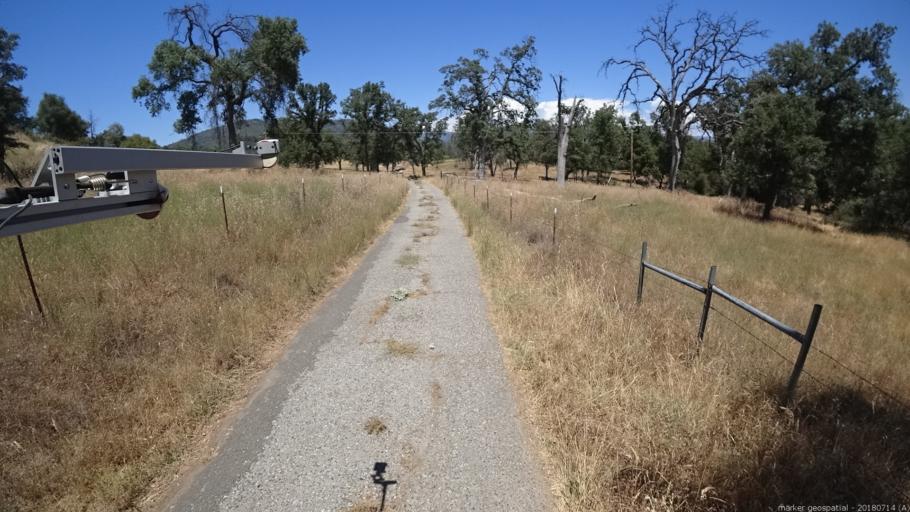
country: US
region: California
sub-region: Madera County
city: Ahwahnee
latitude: 37.3881
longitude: -119.7592
